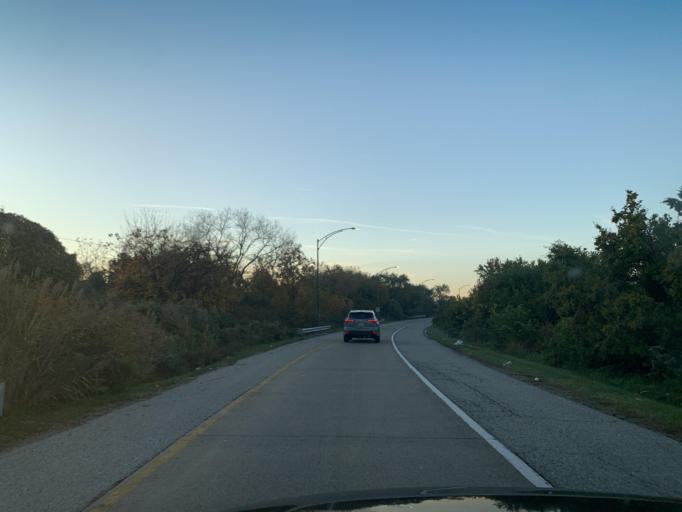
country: US
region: Maryland
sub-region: Baltimore County
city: Rosedale
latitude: 39.3082
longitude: -76.5379
